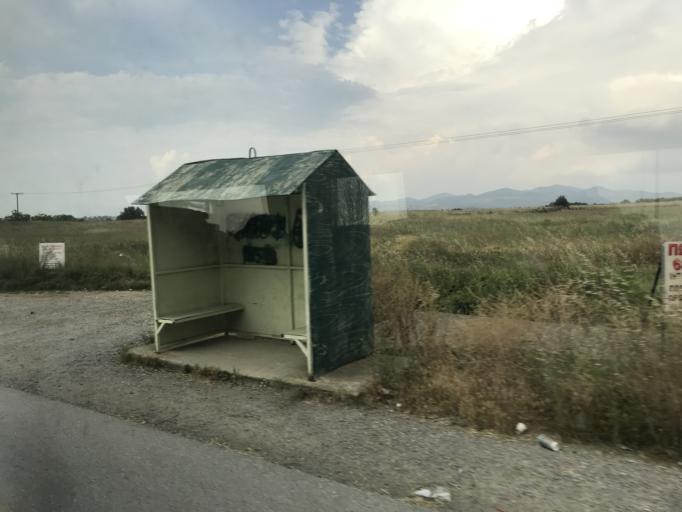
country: GR
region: East Macedonia and Thrace
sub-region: Nomos Rodopis
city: Sapes
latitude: 40.9641
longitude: 25.6446
